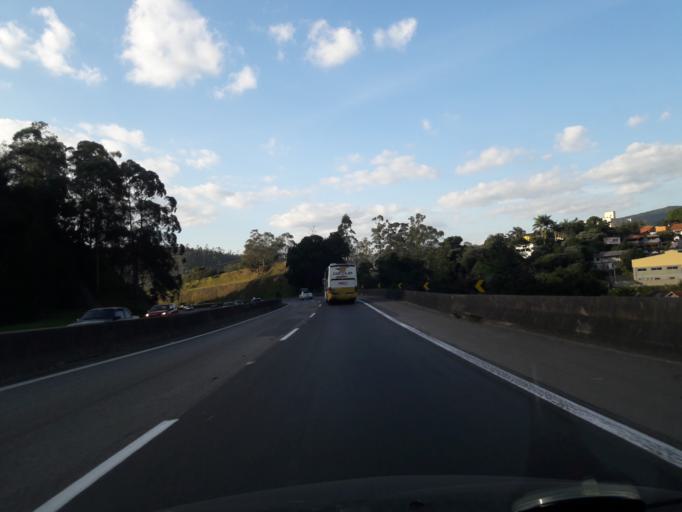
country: BR
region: Sao Paulo
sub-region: Mairipora
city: Mairipora
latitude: -23.2506
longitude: -46.5936
